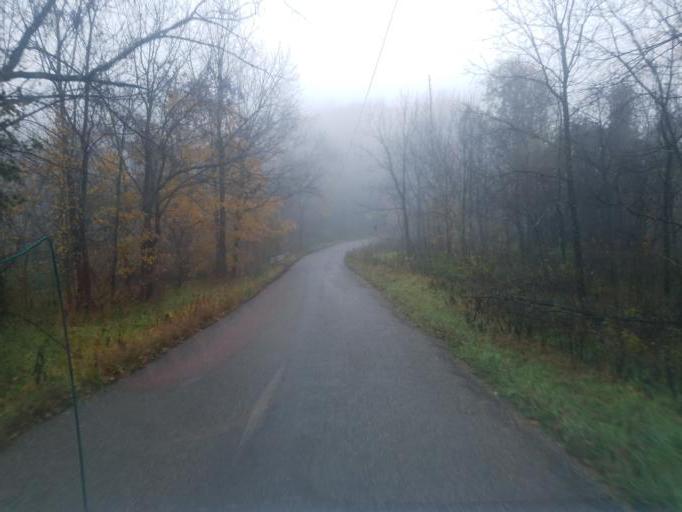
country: US
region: Ohio
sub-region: Athens County
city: Glouster
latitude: 39.4803
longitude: -81.9514
